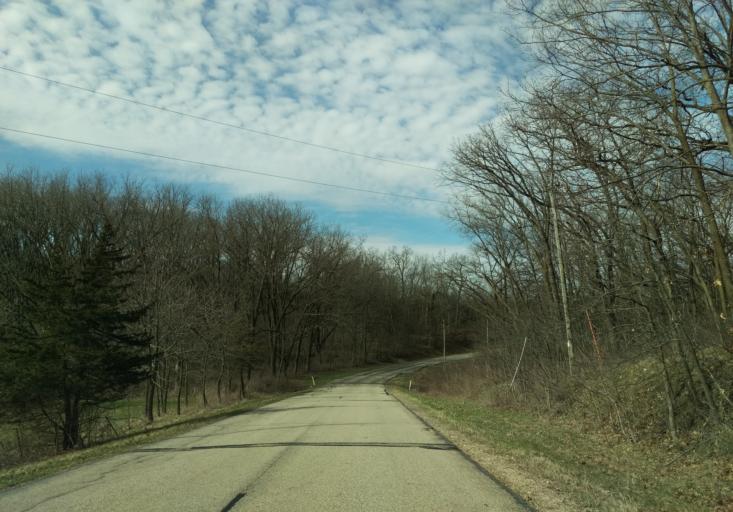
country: US
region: Wisconsin
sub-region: Dane County
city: Mount Horeb
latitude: 43.0552
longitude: -89.7150
